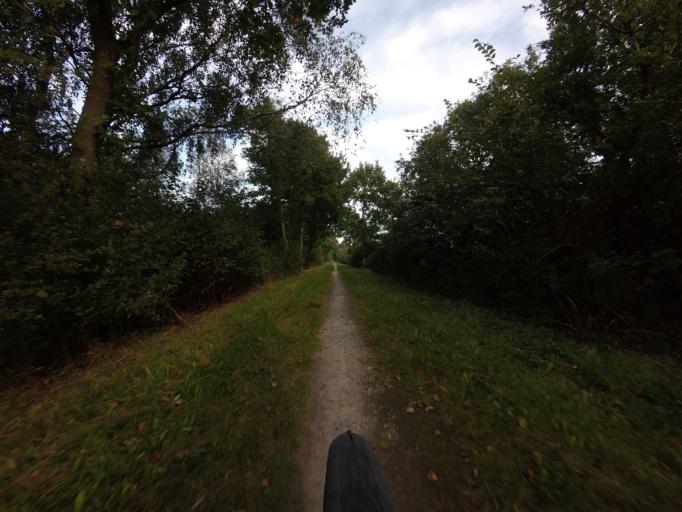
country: DK
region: Central Jutland
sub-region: Ikast-Brande Kommune
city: Brande
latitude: 55.9193
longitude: 9.1097
